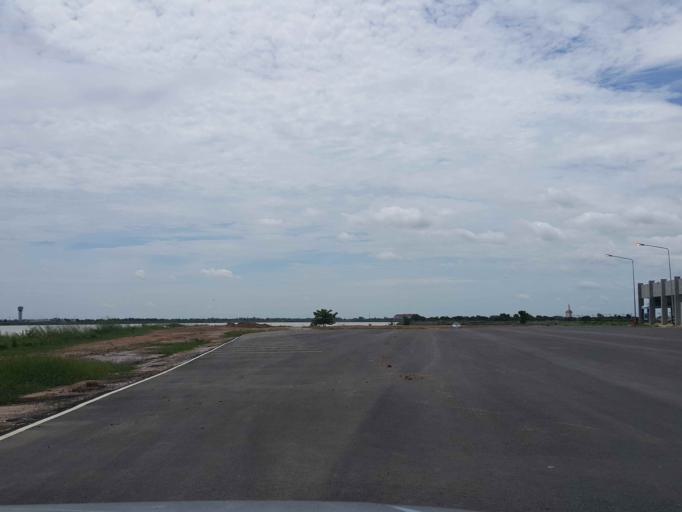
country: TH
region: Sukhothai
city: Sukhothai
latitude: 17.0624
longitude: 99.7948
